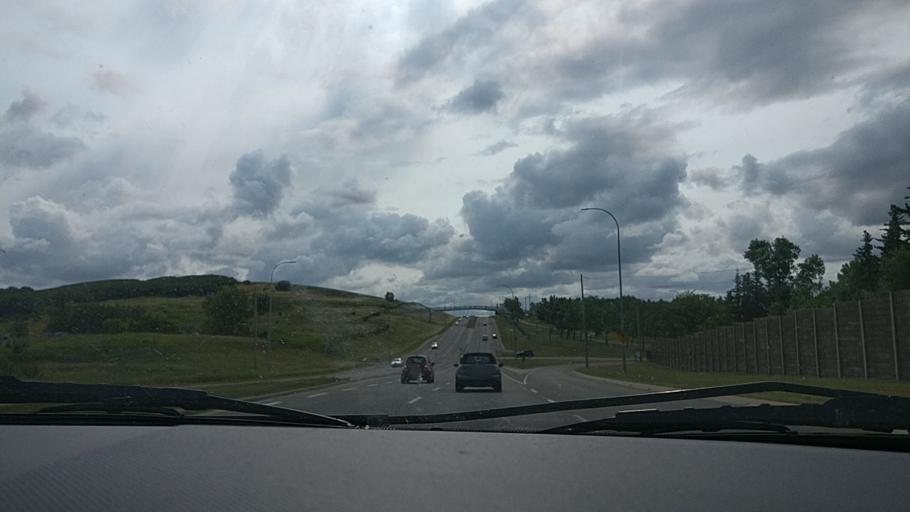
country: CA
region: Alberta
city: Calgary
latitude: 51.1041
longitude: -114.1291
